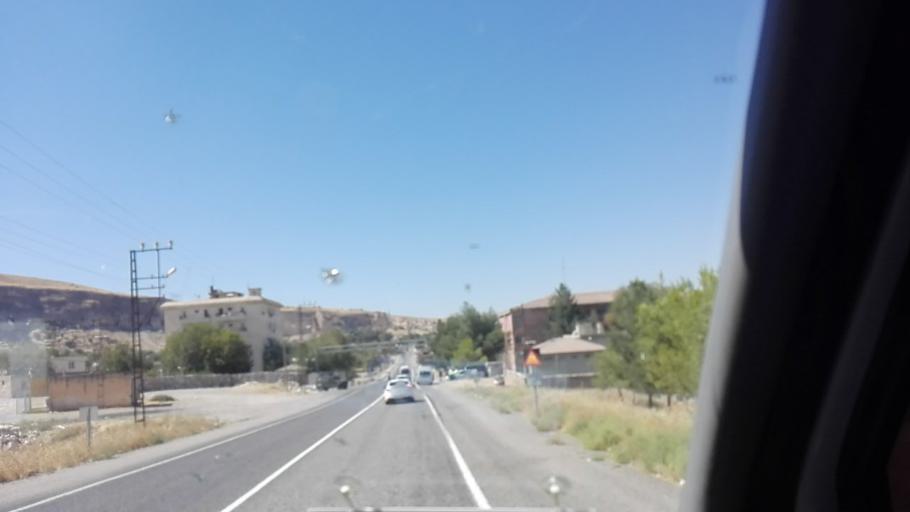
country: TR
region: Batman
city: Hasankeyf
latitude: 37.7136
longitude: 41.4261
